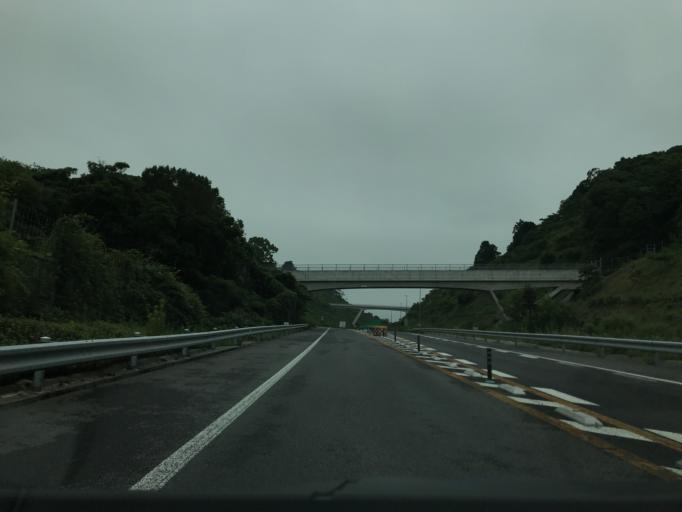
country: JP
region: Fukuoka
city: Nakatsu
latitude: 33.5040
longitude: 131.3033
